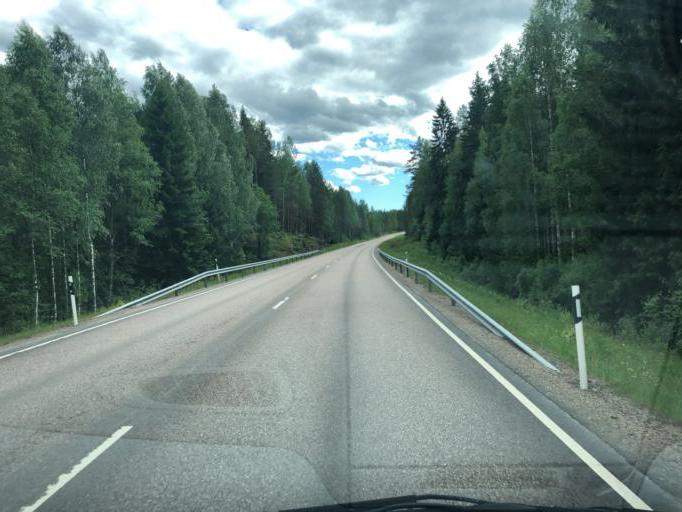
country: FI
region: Southern Savonia
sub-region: Mikkeli
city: Maentyharju
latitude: 61.1268
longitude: 27.1026
